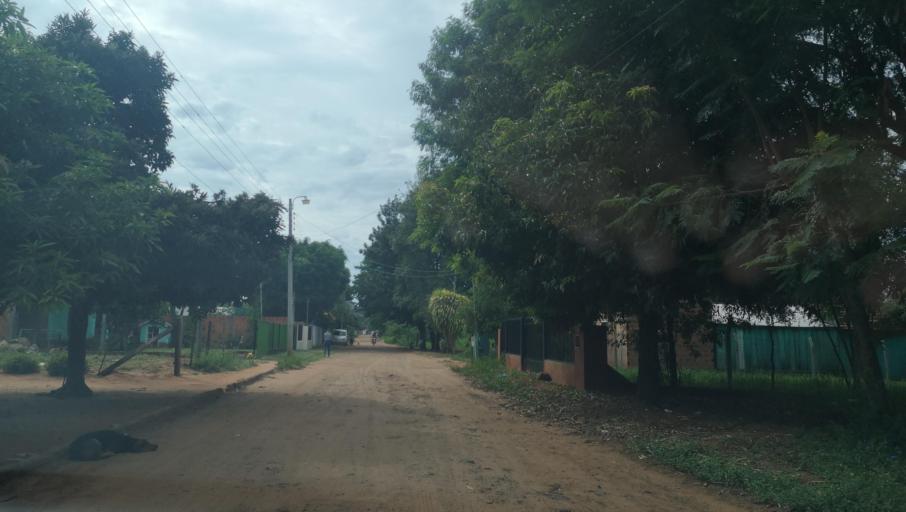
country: PY
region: San Pedro
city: Capiibary
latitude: -24.7270
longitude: -56.0232
